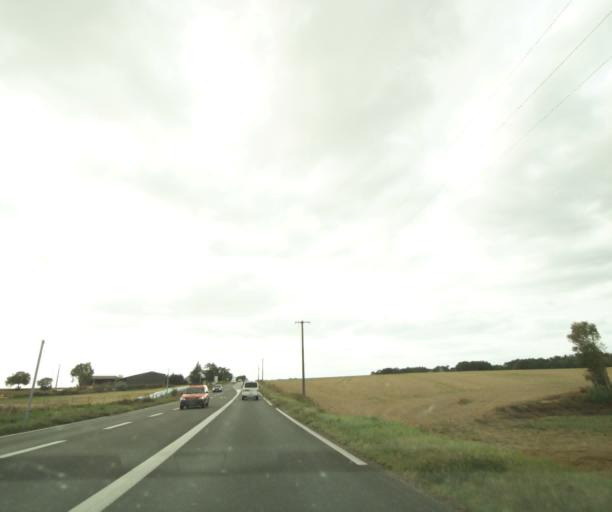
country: FR
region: Centre
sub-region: Departement d'Indre-et-Loire
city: Chambourg-sur-Indre
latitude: 47.1815
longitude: 0.9585
